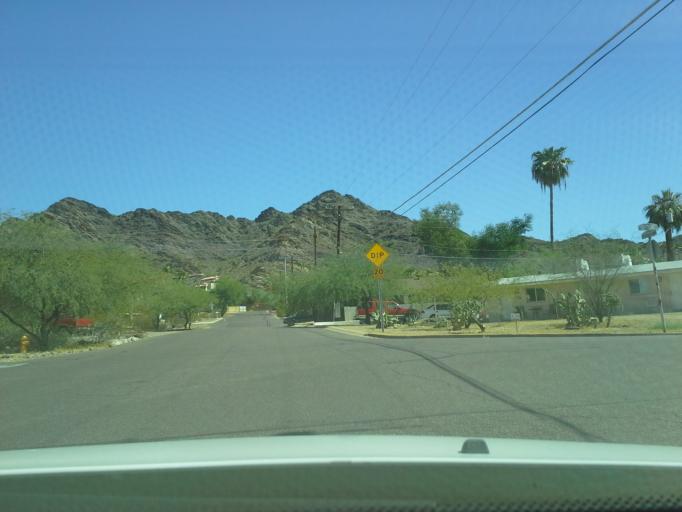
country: US
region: Arizona
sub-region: Maricopa County
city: Paradise Valley
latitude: 33.5748
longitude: -112.0481
